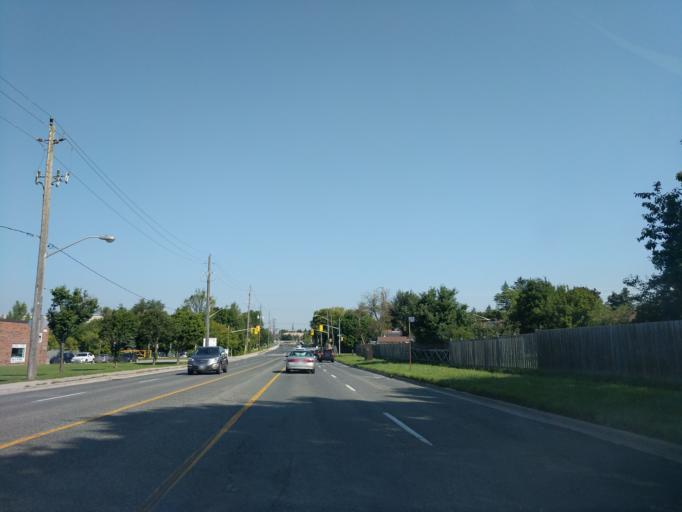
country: CA
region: Ontario
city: Scarborough
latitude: 43.7796
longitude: -79.2757
